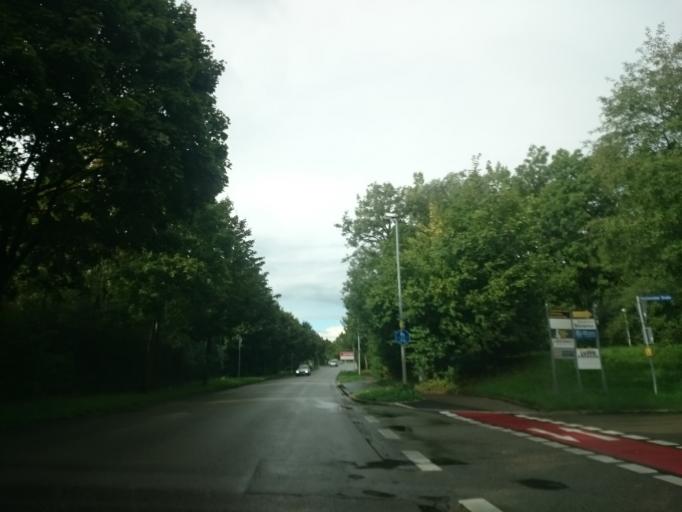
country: DE
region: Bavaria
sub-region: Swabia
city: Kempten (Allgaeu)
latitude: 47.7527
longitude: 10.3169
